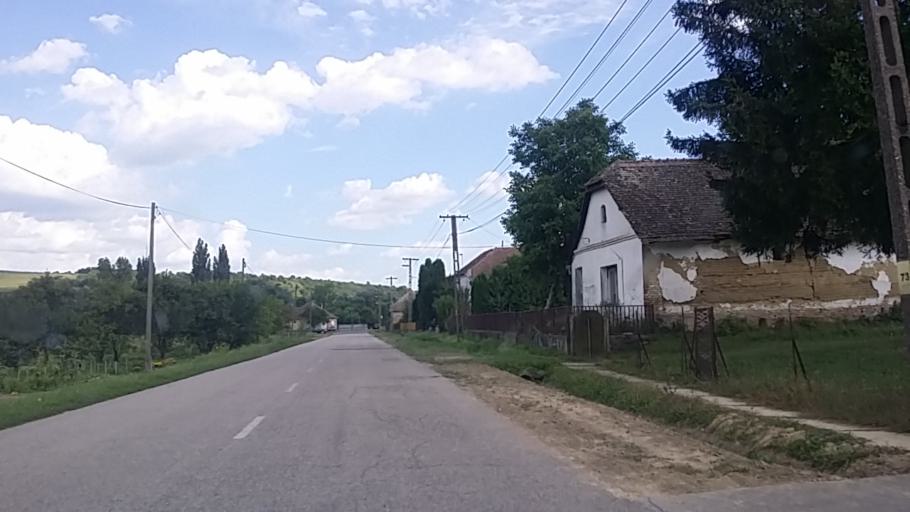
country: HU
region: Tolna
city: Gyonk
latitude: 46.5276
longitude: 18.5127
